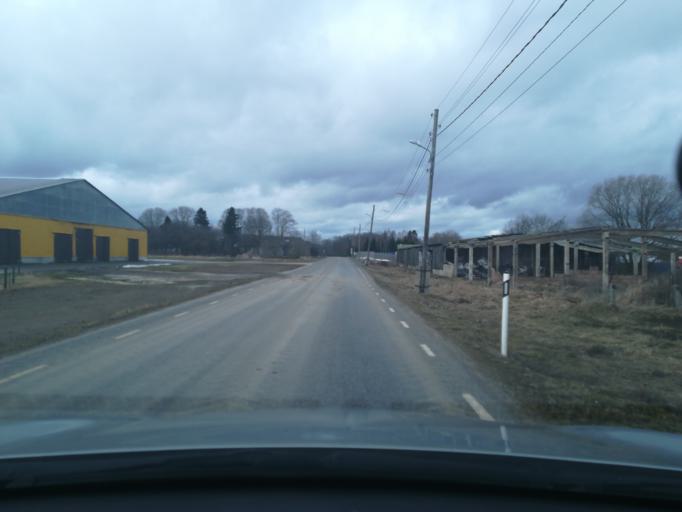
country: EE
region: Harju
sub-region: Saue linn
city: Saue
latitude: 59.3436
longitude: 24.5502
